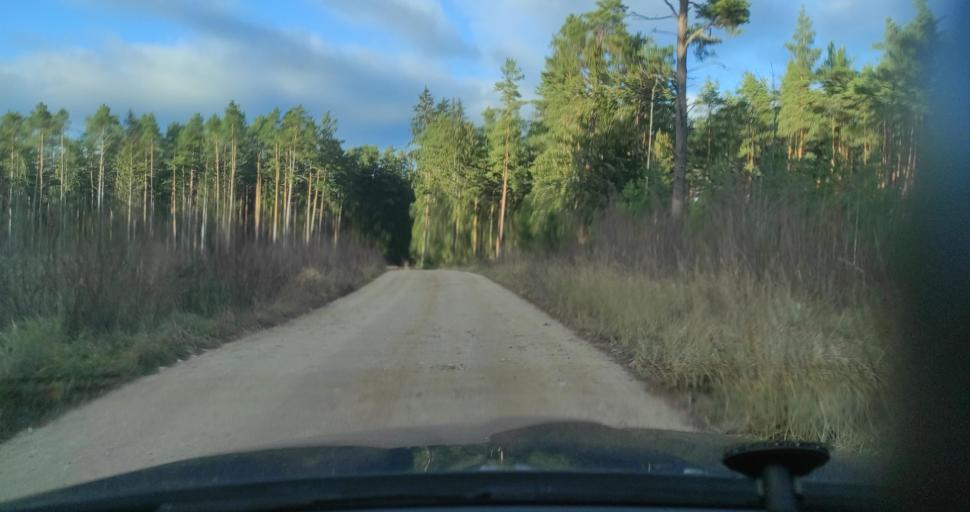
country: LV
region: Kuldigas Rajons
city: Kuldiga
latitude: 57.2823
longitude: 22.0402
